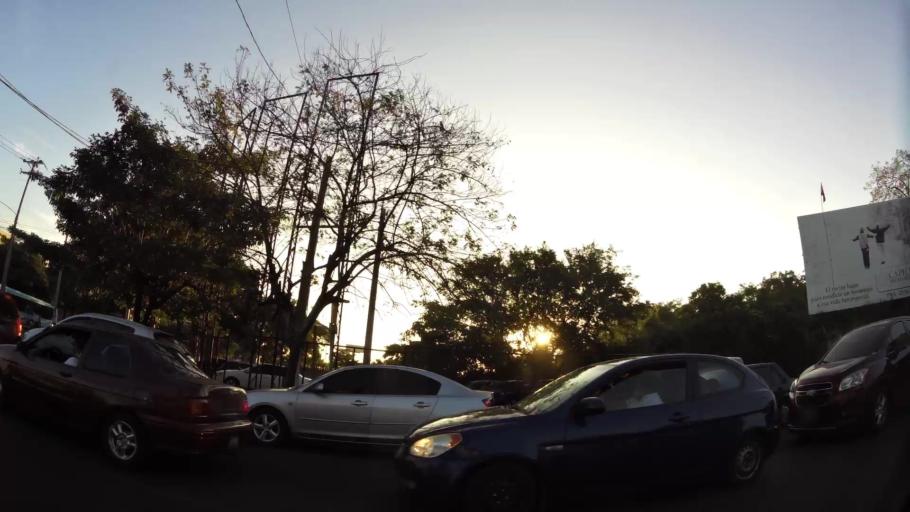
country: SV
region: San Salvador
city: San Salvador
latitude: 13.7041
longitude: -89.2194
